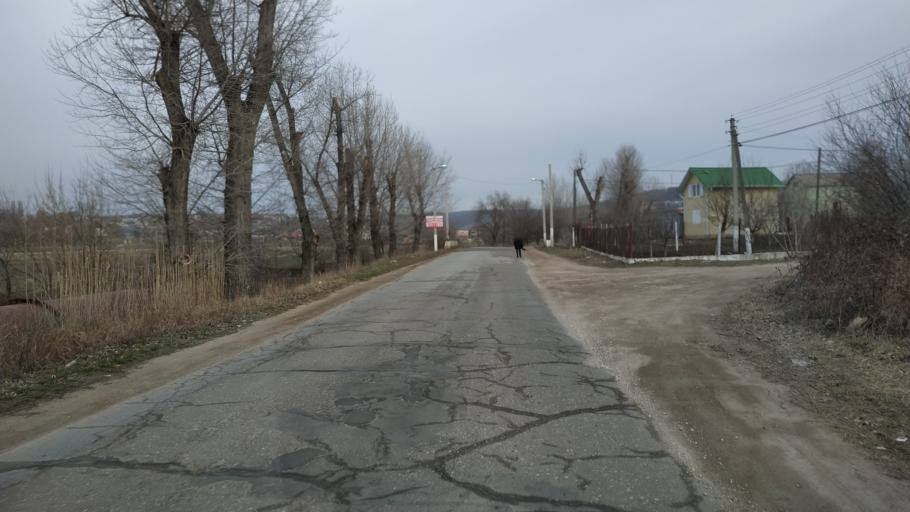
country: MD
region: Chisinau
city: Vatra
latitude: 47.0840
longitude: 28.7698
